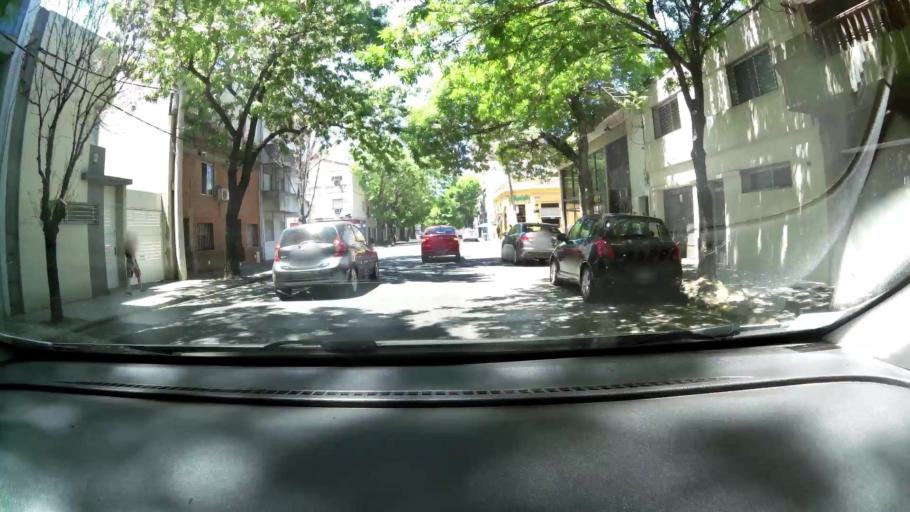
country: AR
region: Santa Fe
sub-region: Departamento de Rosario
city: Rosario
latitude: -32.9452
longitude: -60.6599
